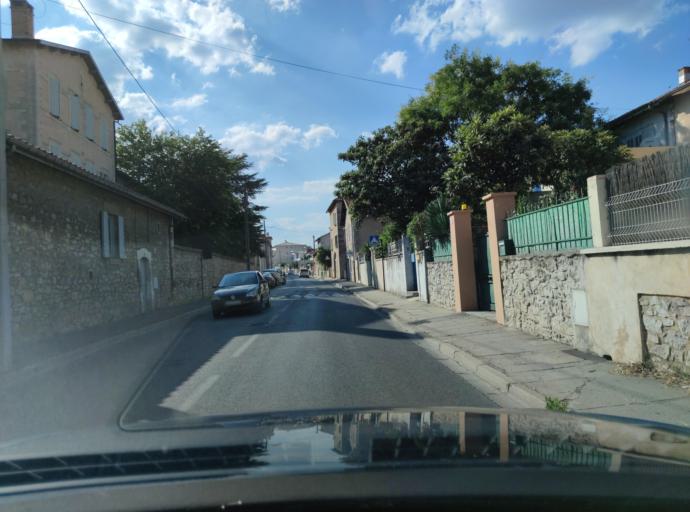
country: FR
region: Languedoc-Roussillon
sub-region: Departement du Gard
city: Nimes
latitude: 43.8348
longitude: 4.3766
